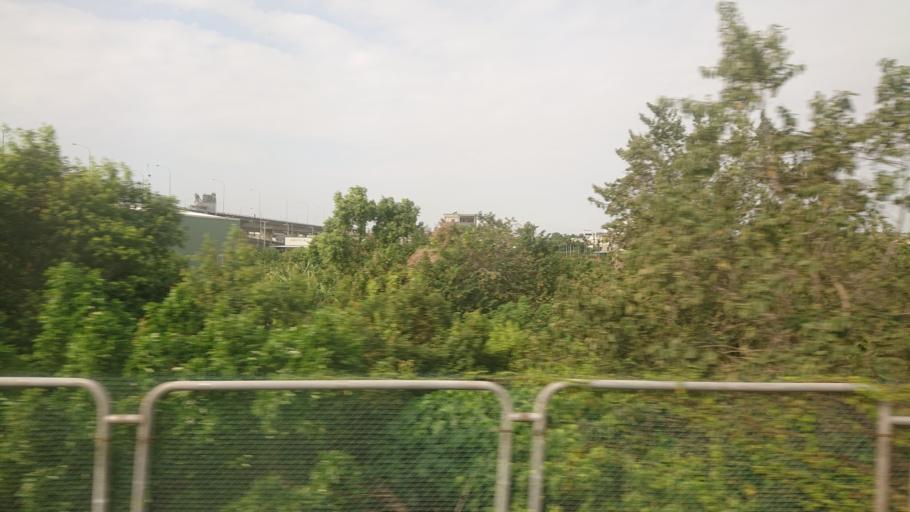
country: TW
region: Taiwan
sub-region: Nantou
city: Nantou
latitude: 23.9459
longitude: 120.5694
